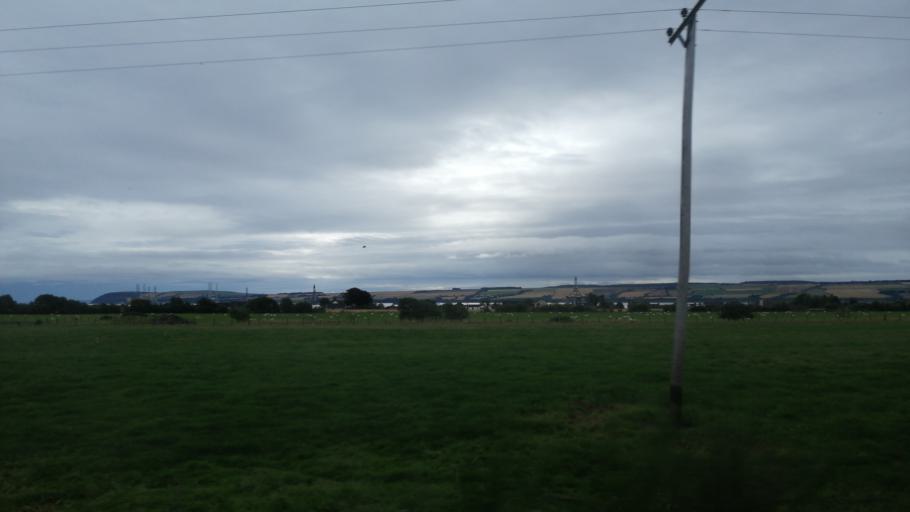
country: GB
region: Scotland
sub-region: Highland
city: Invergordon
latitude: 57.7020
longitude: -4.1480
